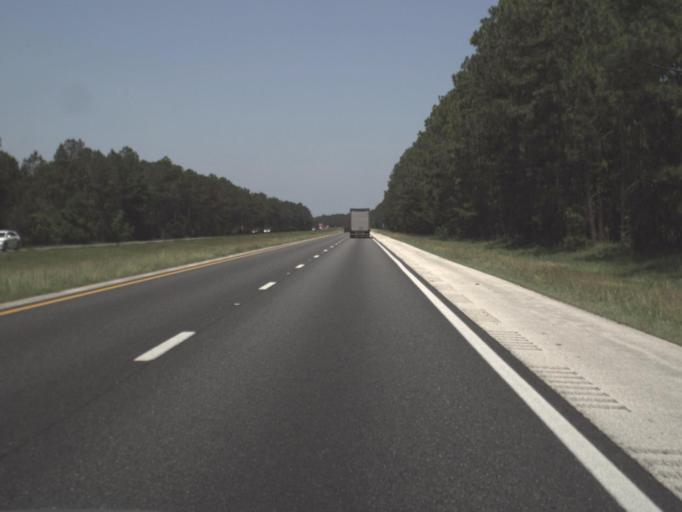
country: US
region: Florida
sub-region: Duval County
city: Baldwin
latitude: 30.2871
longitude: -82.0112
